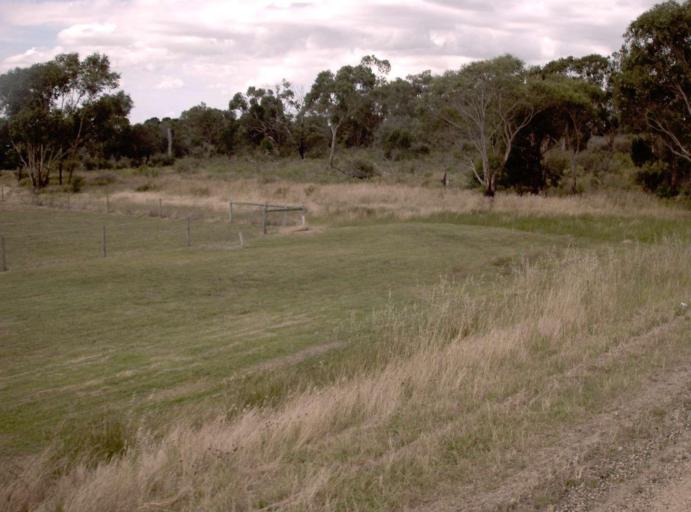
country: AU
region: Victoria
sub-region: Wellington
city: Sale
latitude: -38.1724
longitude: 147.0088
